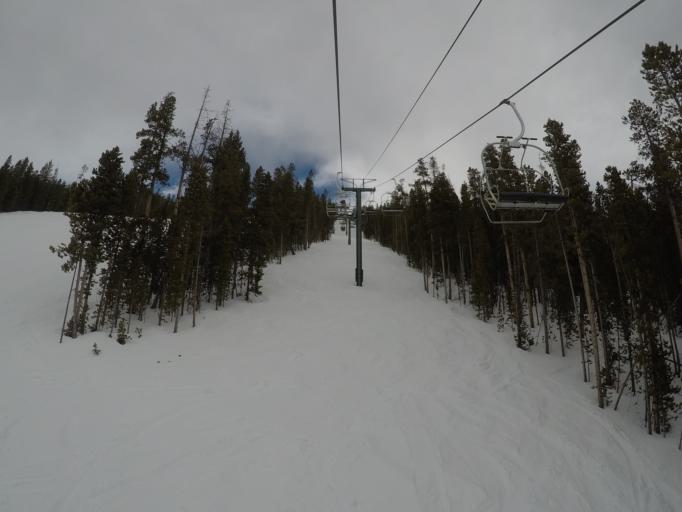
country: US
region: Montana
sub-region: Granite County
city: Philipsburg
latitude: 46.2561
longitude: -113.2439
